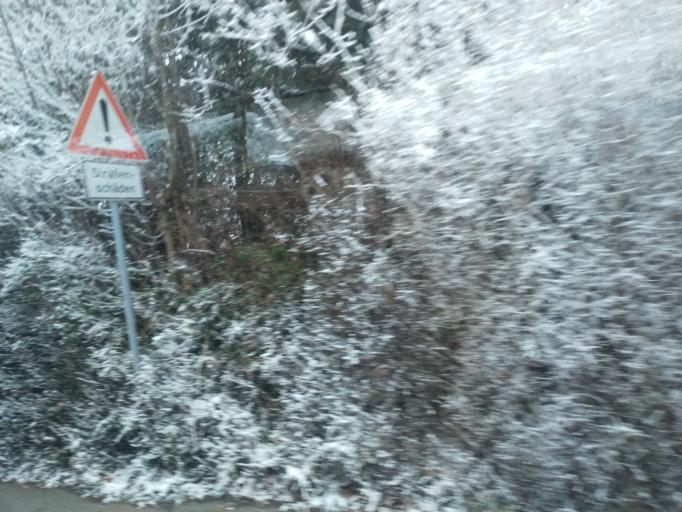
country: DE
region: Baden-Wuerttemberg
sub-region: Karlsruhe Region
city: Neuenburg
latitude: 48.8529
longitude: 8.5836
